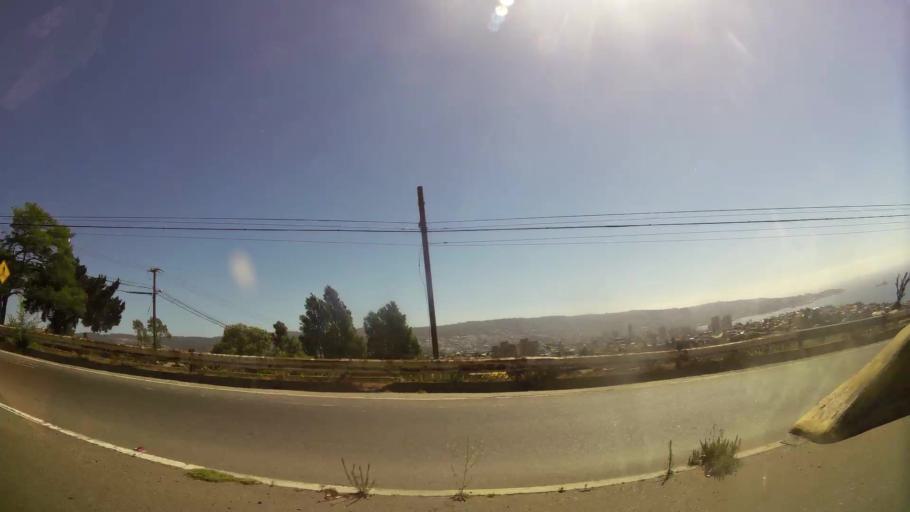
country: CL
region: Valparaiso
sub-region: Provincia de Valparaiso
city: Vina del Mar
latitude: -33.0420
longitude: -71.5697
